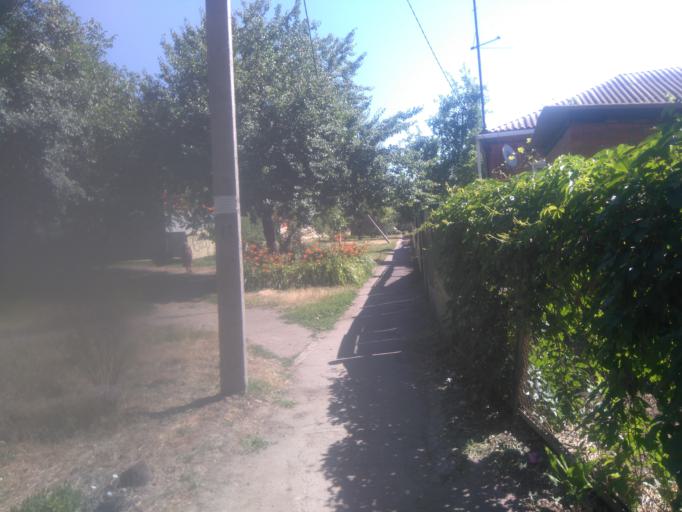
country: RU
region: Krasnodarskiy
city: Fastovetskaya
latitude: 45.9163
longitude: 40.1543
